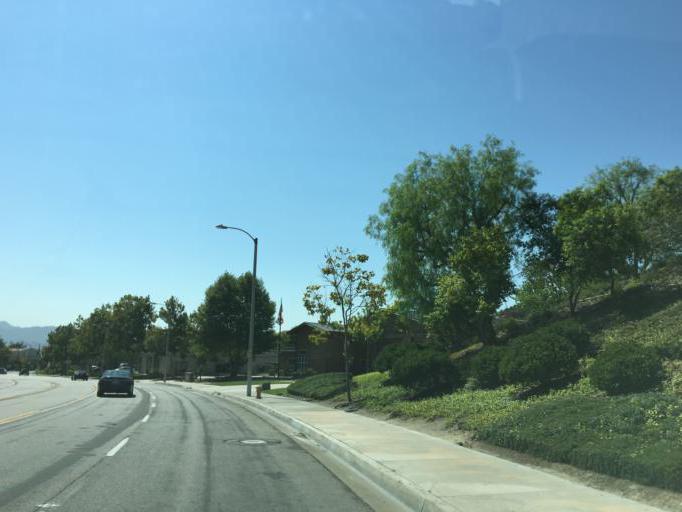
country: US
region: California
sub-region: Los Angeles County
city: Santa Clarita
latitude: 34.3881
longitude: -118.5826
